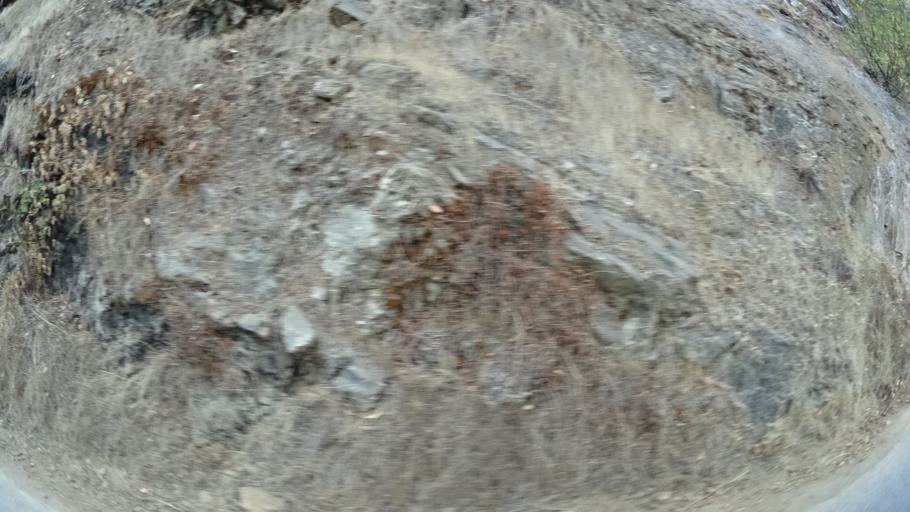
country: US
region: California
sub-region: Siskiyou County
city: Happy Camp
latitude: 41.7778
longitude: -123.3474
